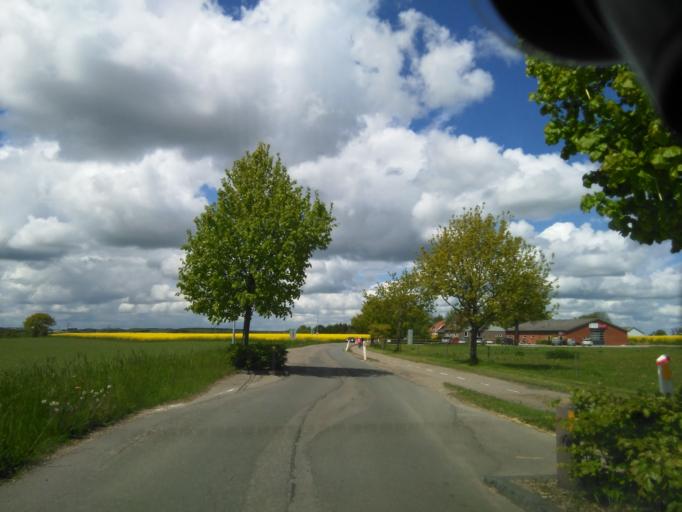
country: DK
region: Central Jutland
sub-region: Arhus Kommune
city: Solbjerg
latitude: 56.0676
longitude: 10.0672
